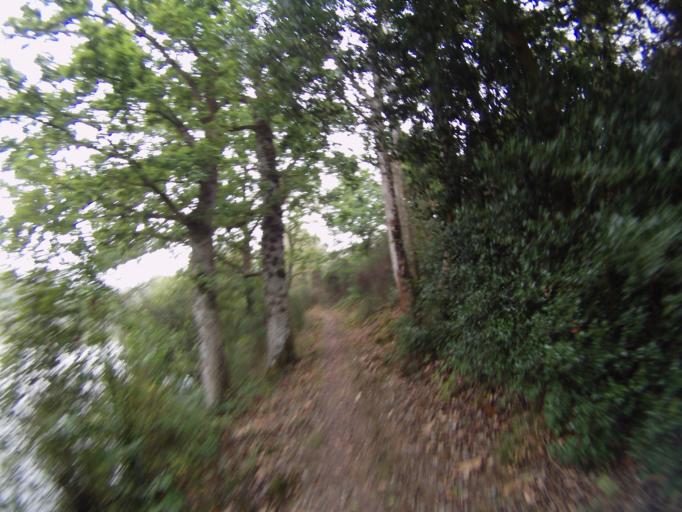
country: FR
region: Brittany
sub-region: Departement d'Ille-et-Vilaine
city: Chanteloup
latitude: 47.9727
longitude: -1.6066
